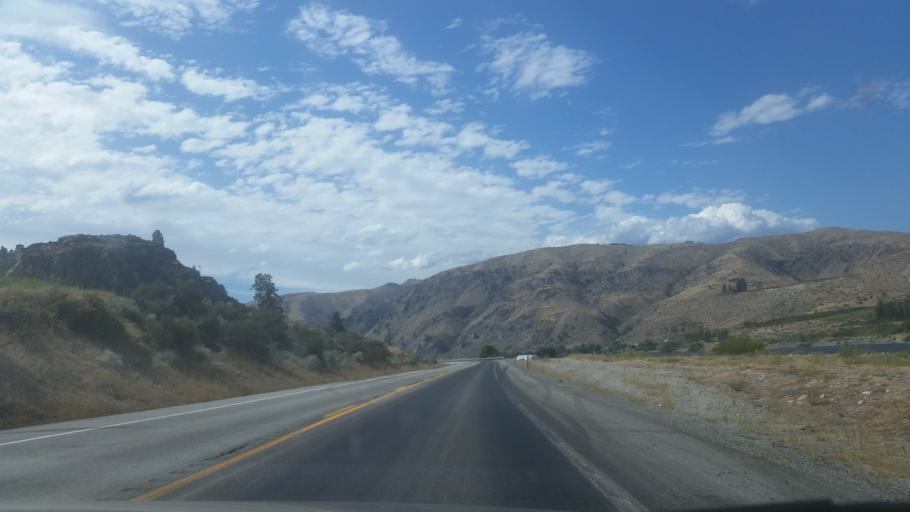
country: US
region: Washington
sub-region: Chelan County
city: Chelan
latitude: 47.7637
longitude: -120.0995
